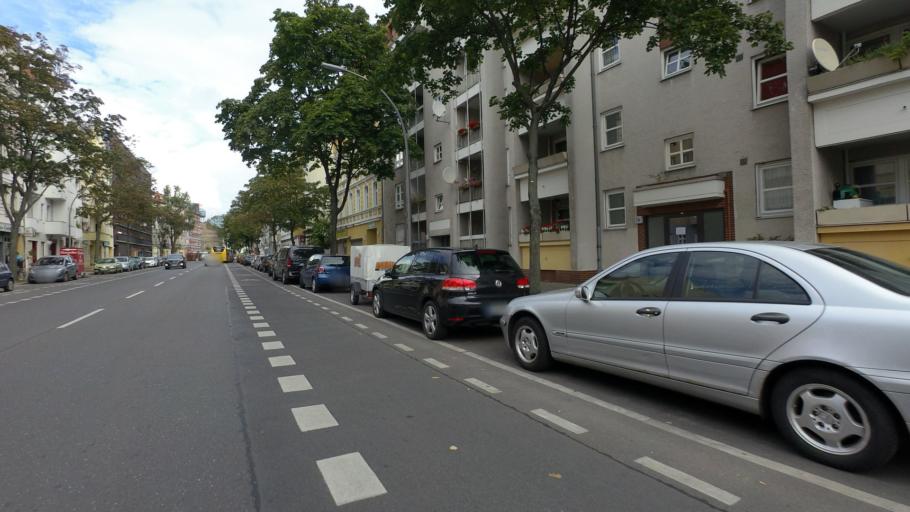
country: DE
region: Berlin
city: Gesundbrunnen
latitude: 52.5592
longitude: 13.3770
